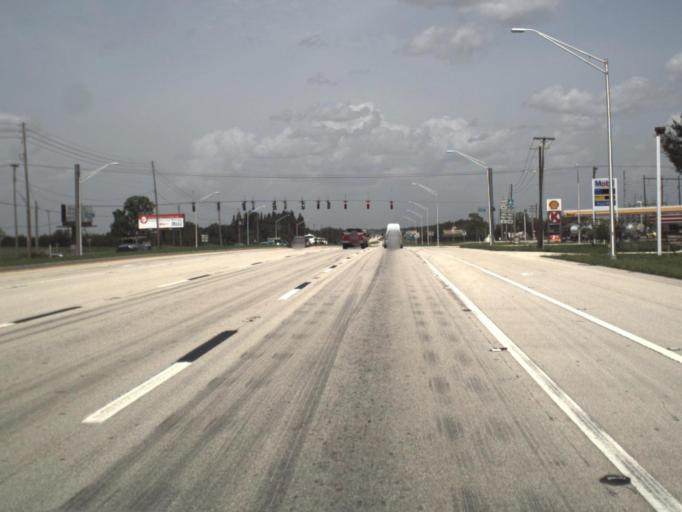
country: US
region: Florida
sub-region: Highlands County
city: Sebring
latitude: 27.4278
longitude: -81.4178
